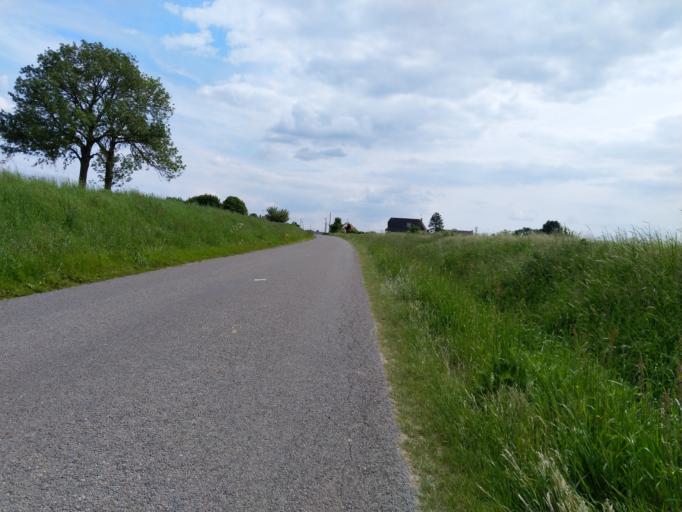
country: FR
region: Picardie
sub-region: Departement de l'Aisne
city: Boue
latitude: 50.0172
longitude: 3.6927
